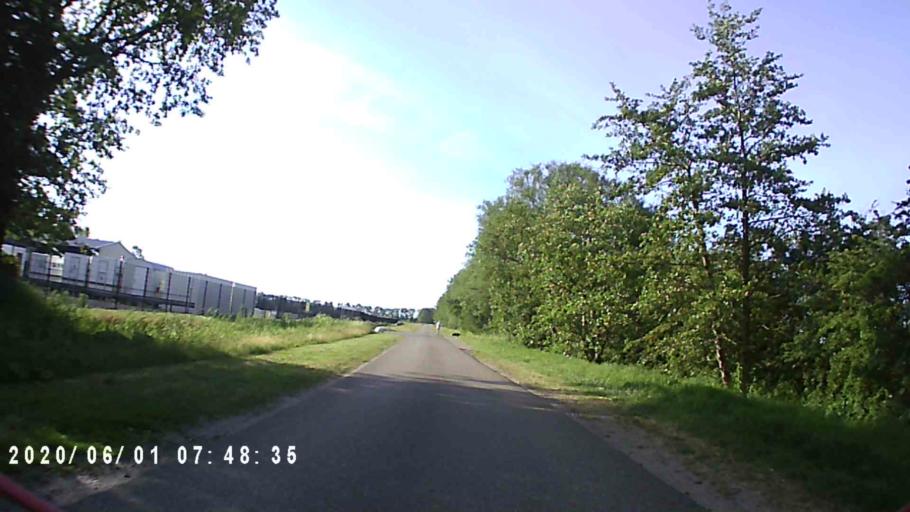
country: NL
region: Friesland
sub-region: Gemeente Dantumadiel
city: Rinsumageast
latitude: 53.2933
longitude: 5.9527
